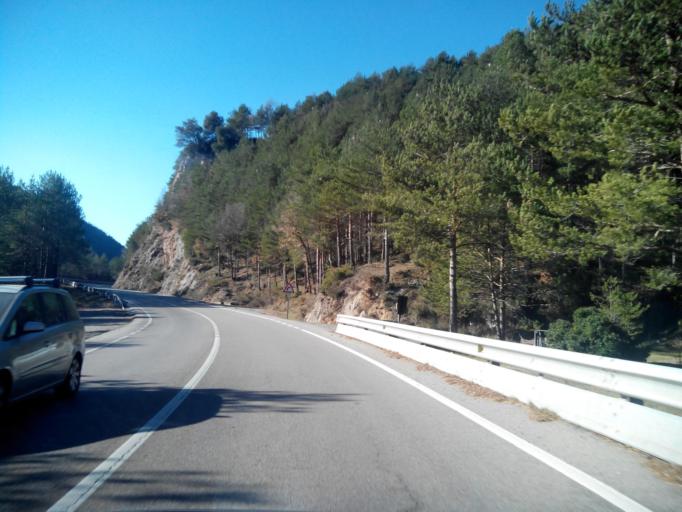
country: ES
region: Catalonia
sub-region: Provincia de Barcelona
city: Vilada
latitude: 42.1293
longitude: 1.8963
